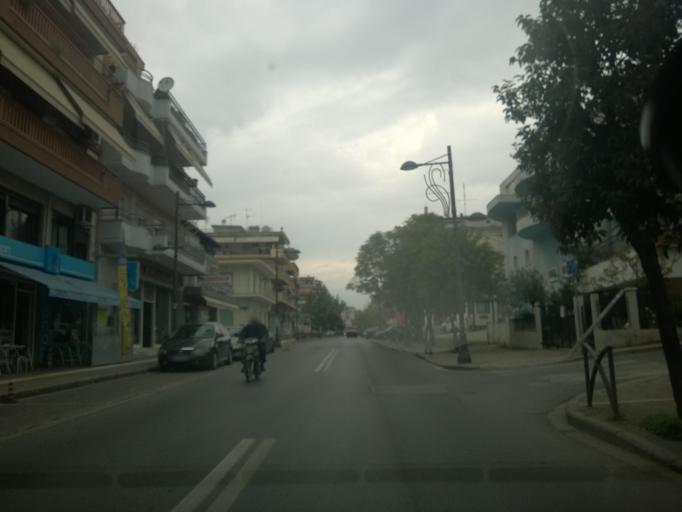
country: GR
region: Central Macedonia
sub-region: Nomos Thessalonikis
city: Stavroupoli
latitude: 40.6702
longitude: 22.9333
